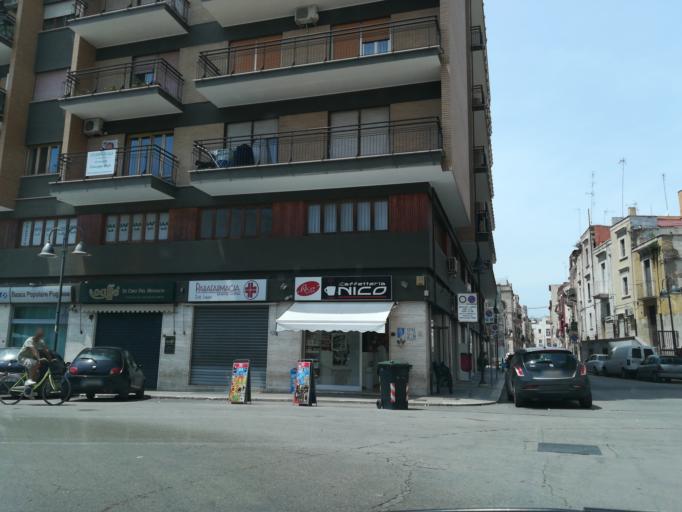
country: IT
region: Apulia
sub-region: Provincia di Barletta - Andria - Trani
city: Barletta
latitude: 41.3191
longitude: 16.2786
